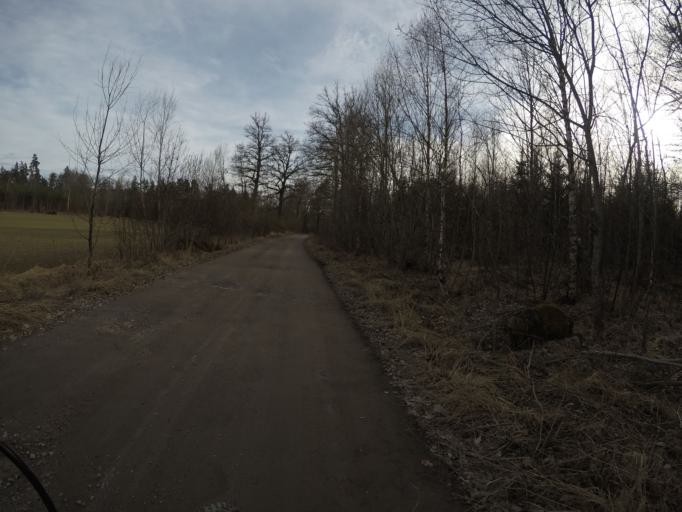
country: SE
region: Soedermanland
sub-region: Eskilstuna Kommun
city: Kvicksund
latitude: 59.4398
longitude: 16.3727
